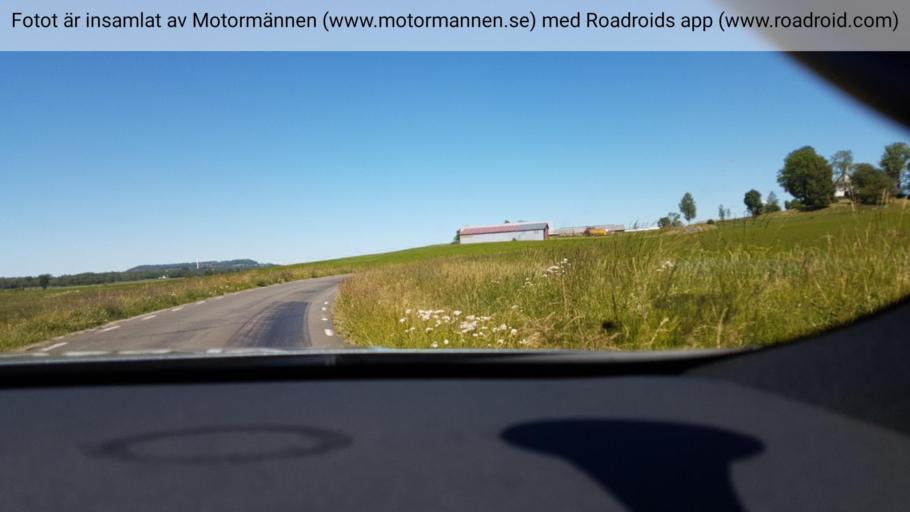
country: SE
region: Vaestra Goetaland
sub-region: Falkopings Kommun
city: Falkoeping
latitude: 58.0719
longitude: 13.5534
